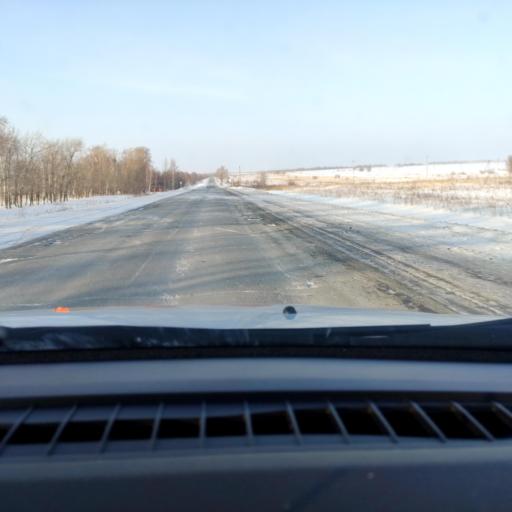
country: RU
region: Samara
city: Dubovyy Umet
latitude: 53.0914
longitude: 50.3495
